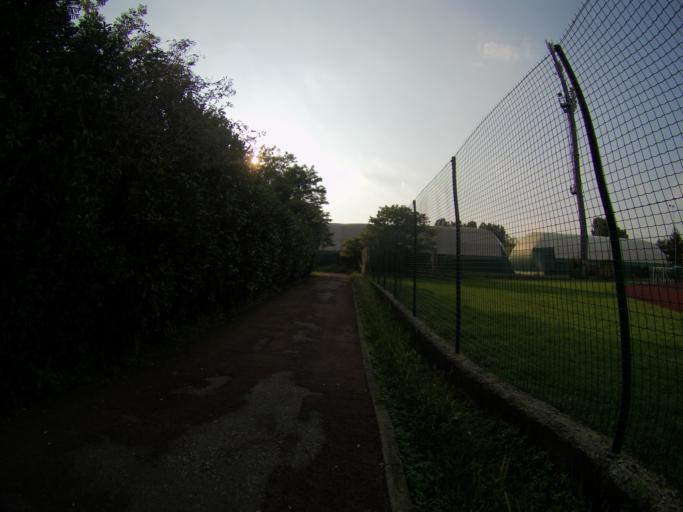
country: IT
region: Lombardy
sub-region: Citta metropolitana di Milano
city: Vignate
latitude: 45.4917
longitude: 9.3787
